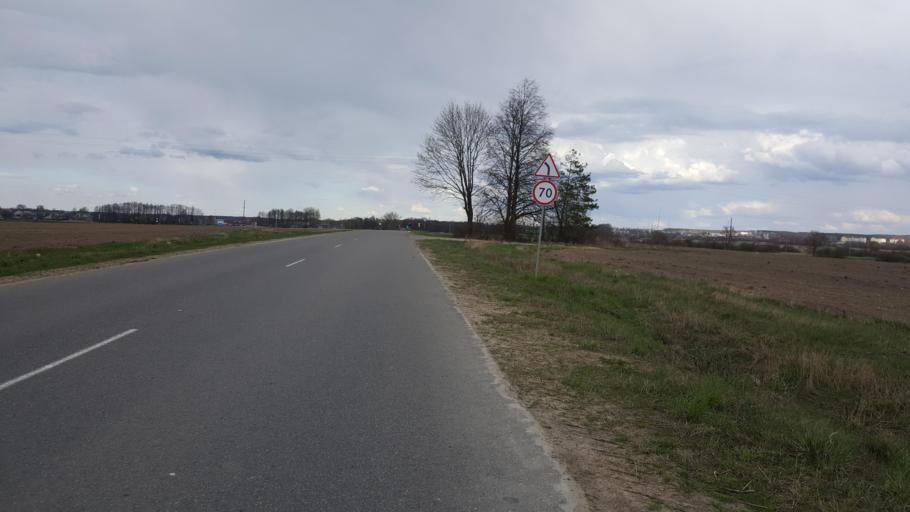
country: BY
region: Brest
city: Kamyanyets
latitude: 52.3970
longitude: 23.7792
